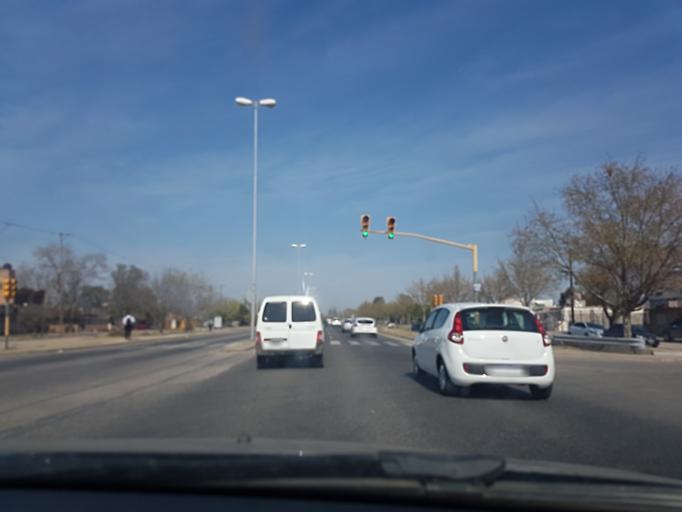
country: AR
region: Cordoba
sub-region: Departamento de Capital
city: Cordoba
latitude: -31.4794
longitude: -64.2392
